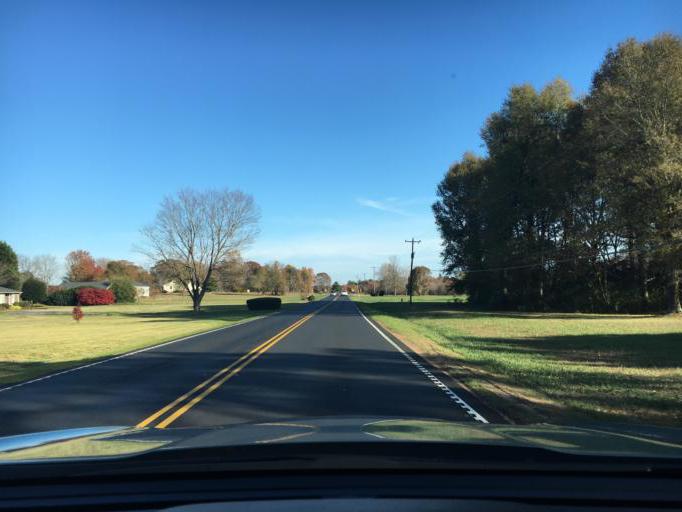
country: US
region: South Carolina
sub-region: Spartanburg County
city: Inman Mills
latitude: 35.0248
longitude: -82.0899
